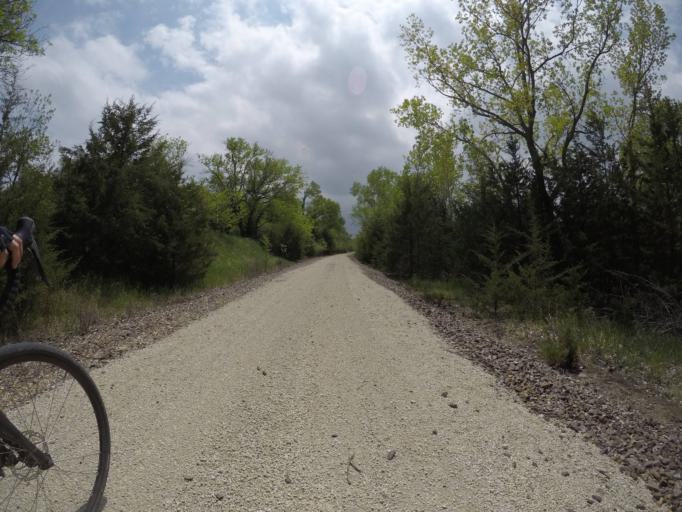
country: US
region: Nebraska
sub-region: Gage County
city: Wymore
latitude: 40.2024
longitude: -96.6606
